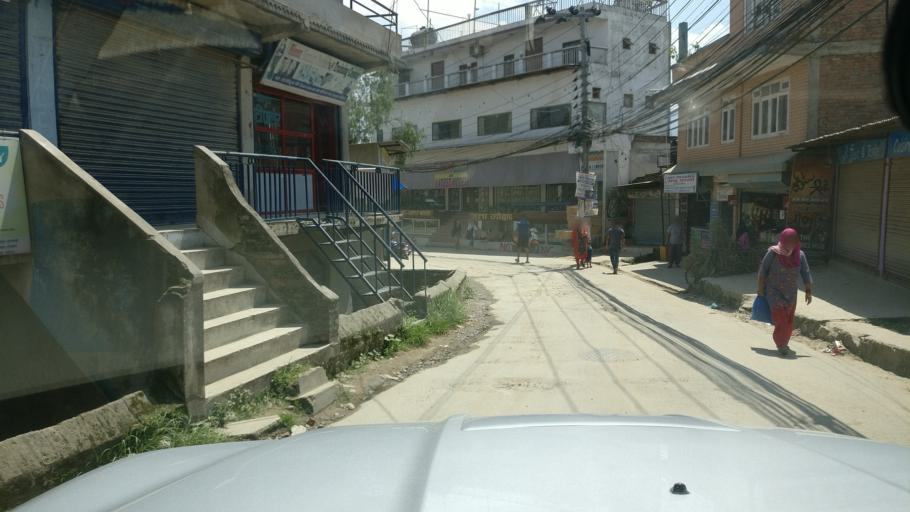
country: NP
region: Central Region
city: Kirtipur
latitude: 27.6939
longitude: 85.2776
